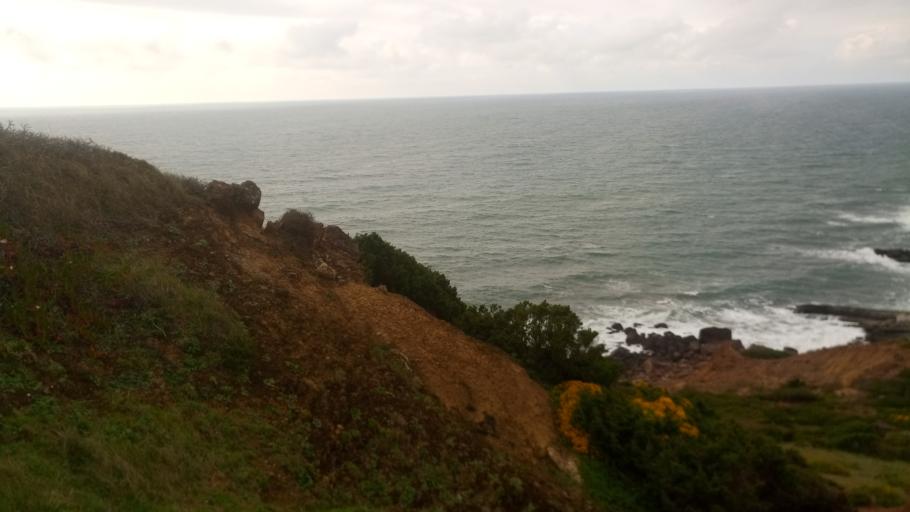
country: PT
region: Leiria
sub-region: Caldas da Rainha
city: Caldas da Rainha
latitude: 39.4876
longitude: -9.1813
